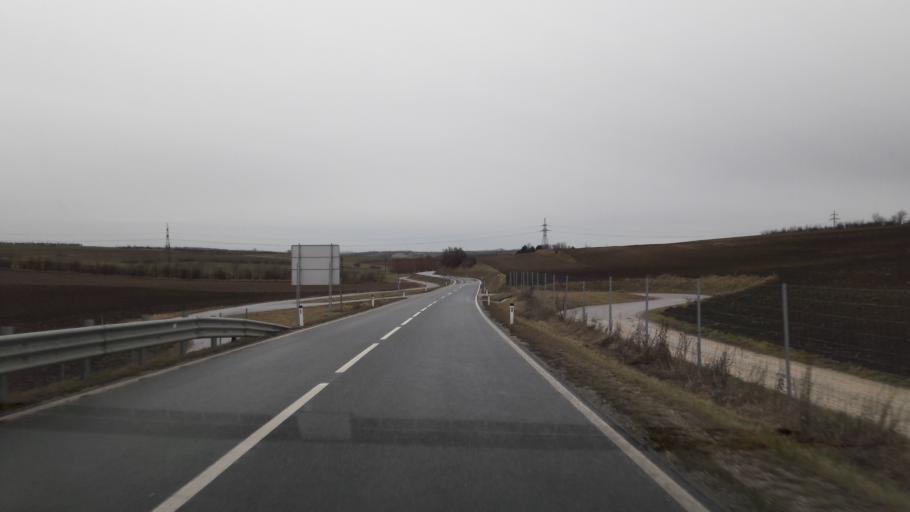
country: AT
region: Lower Austria
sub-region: Politischer Bezirk Mistelbach
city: Hochleithen
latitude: 48.4320
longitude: 16.5473
